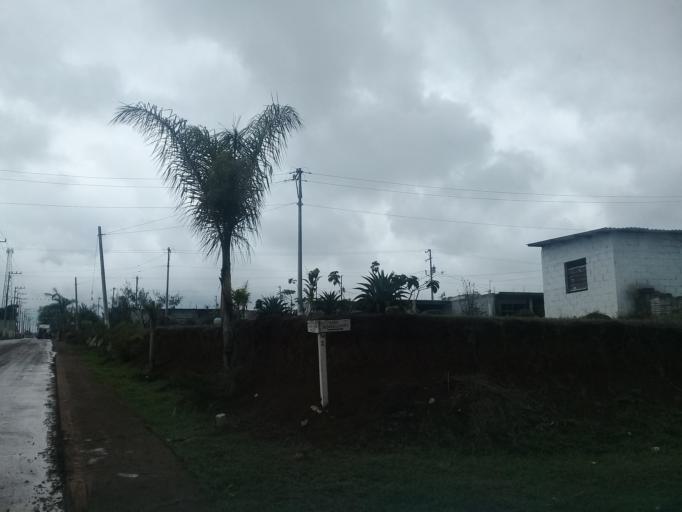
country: MX
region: Veracruz
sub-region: Cordoba
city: San Jose de Tapia
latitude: 18.8499
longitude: -96.9557
